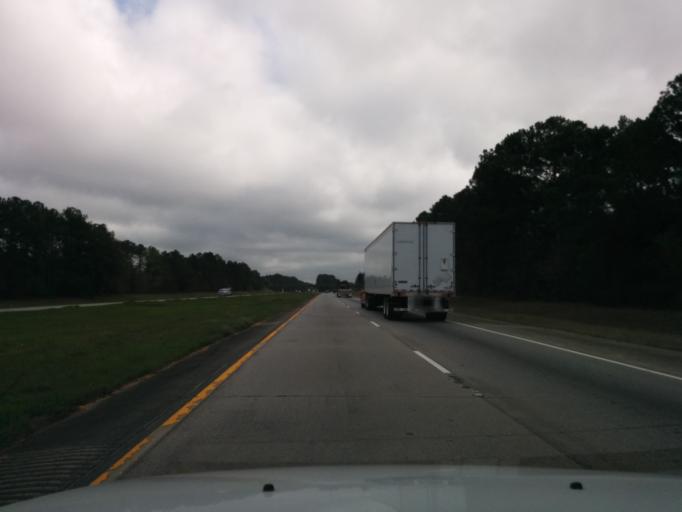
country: US
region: Georgia
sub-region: Toombs County
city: Lyons
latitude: 32.3885
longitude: -82.2736
